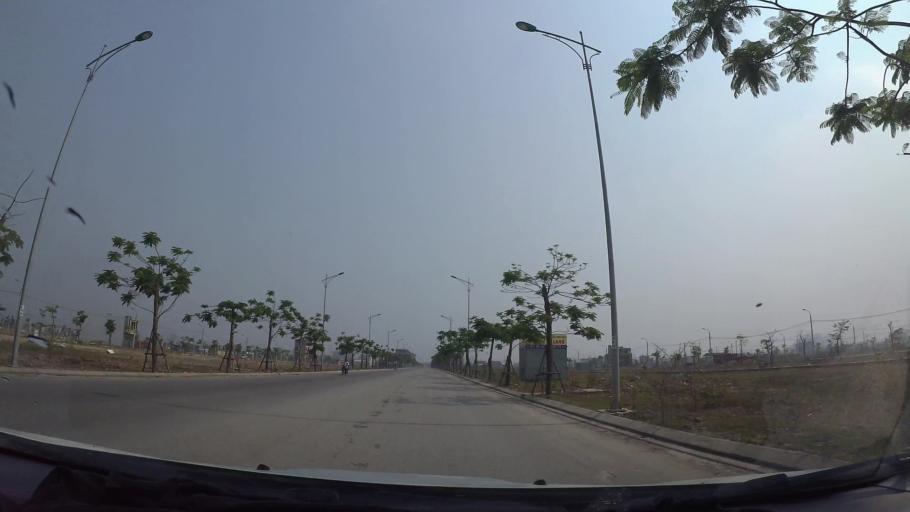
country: VN
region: Da Nang
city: Ngu Hanh Son
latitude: 16.0039
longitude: 108.2380
